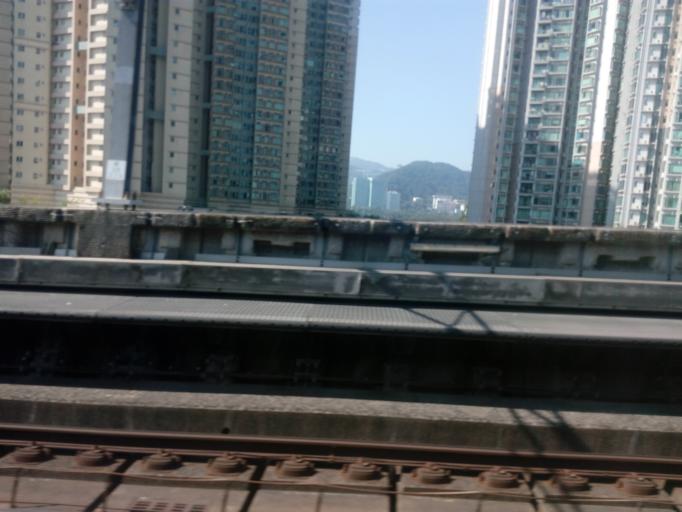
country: HK
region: Sha Tin
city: Sha Tin
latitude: 22.4108
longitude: 114.2235
